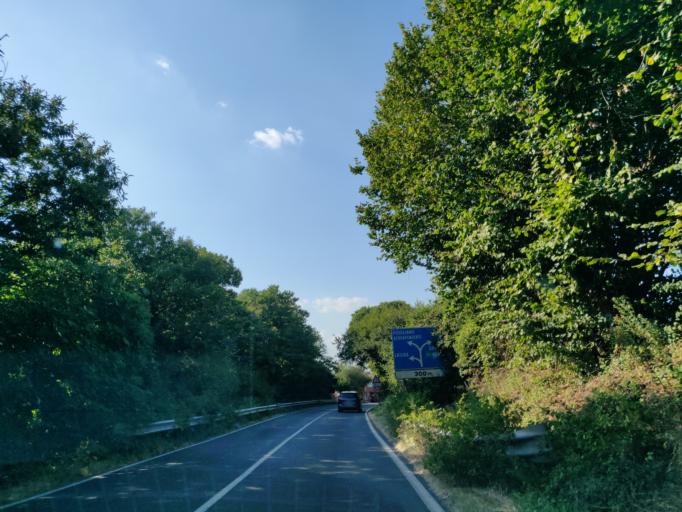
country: IT
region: Latium
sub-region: Provincia di Viterbo
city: Latera
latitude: 42.6295
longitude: 11.8362
